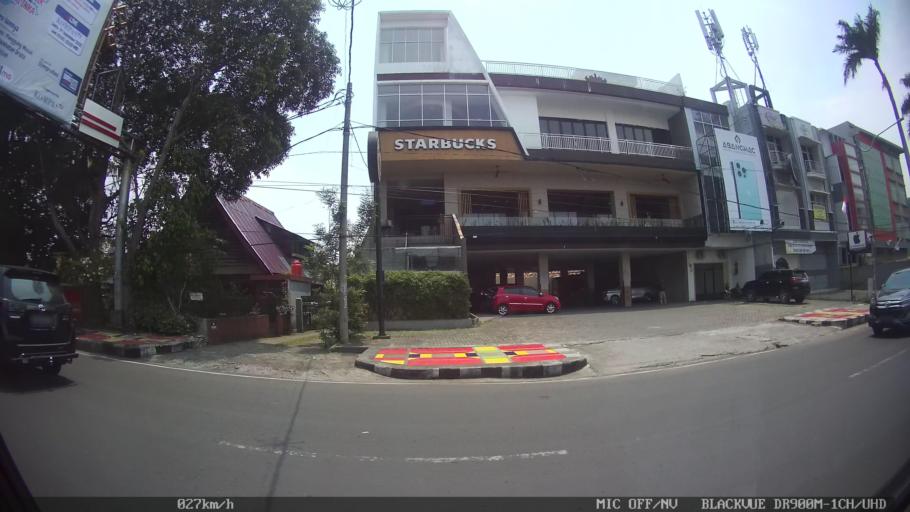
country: ID
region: Lampung
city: Bandarlampung
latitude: -5.4221
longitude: 105.2566
